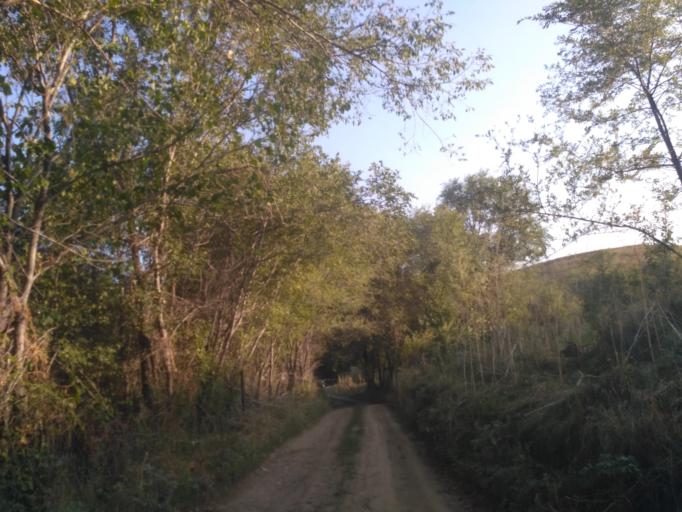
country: KZ
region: Almaty Oblysy
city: Burunday
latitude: 43.1527
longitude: 76.3709
